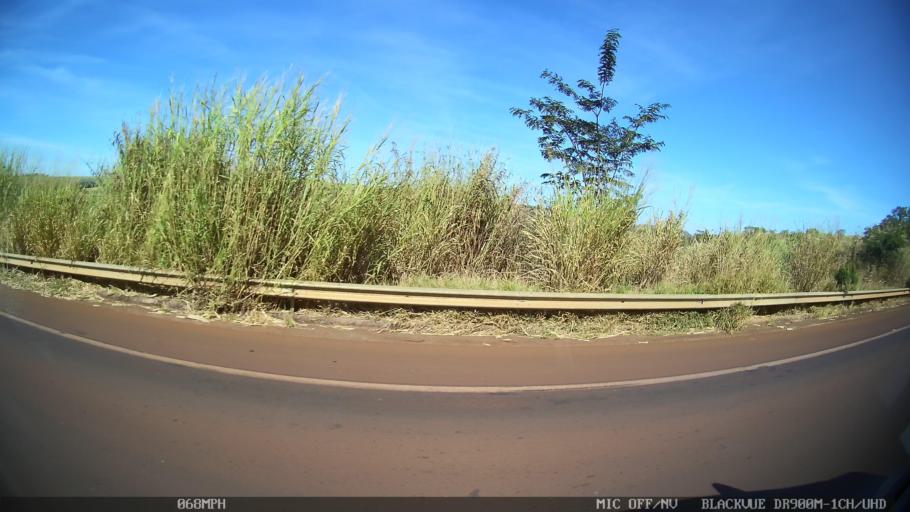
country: BR
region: Sao Paulo
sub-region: Sao Joaquim Da Barra
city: Sao Joaquim da Barra
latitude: -20.5541
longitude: -47.6801
